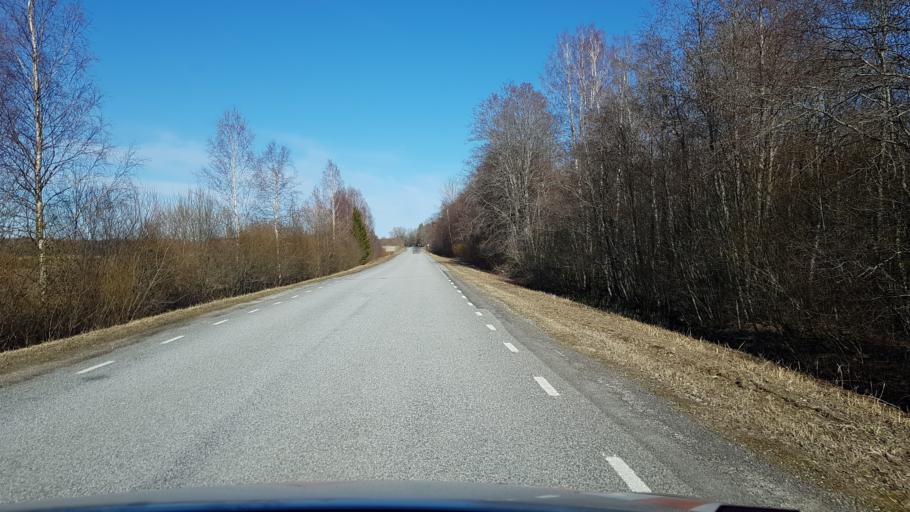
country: EE
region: Laeaene-Virumaa
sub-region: Kadrina vald
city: Kadrina
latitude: 59.3466
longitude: 26.0969
